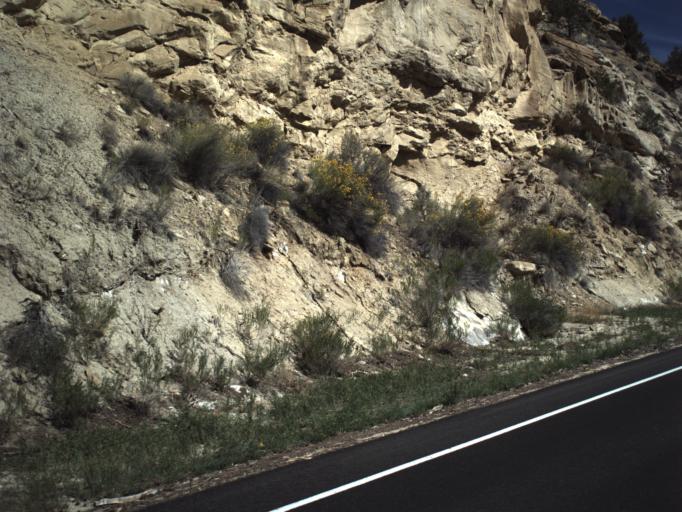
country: US
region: Utah
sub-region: Garfield County
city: Panguitch
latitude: 37.6082
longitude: -111.9038
